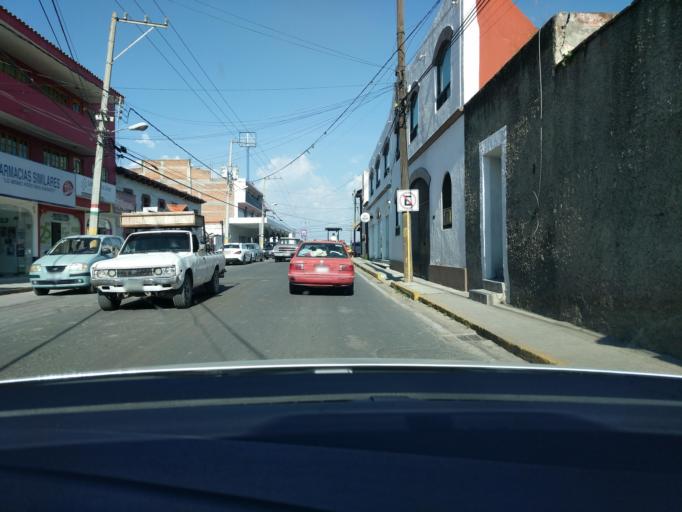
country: MX
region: Puebla
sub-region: San Gregorio Atzompa
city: Chipilo de Francisco Javier Mina
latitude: 19.0055
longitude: -98.3322
